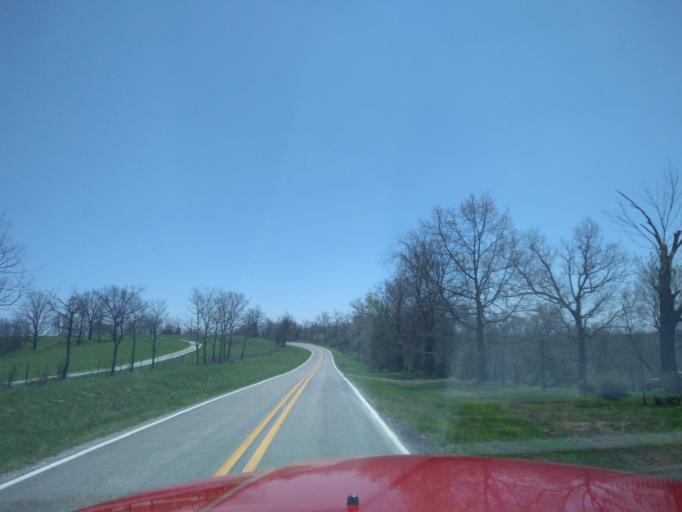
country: US
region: Arkansas
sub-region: Washington County
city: West Fork
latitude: 35.8210
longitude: -94.2627
